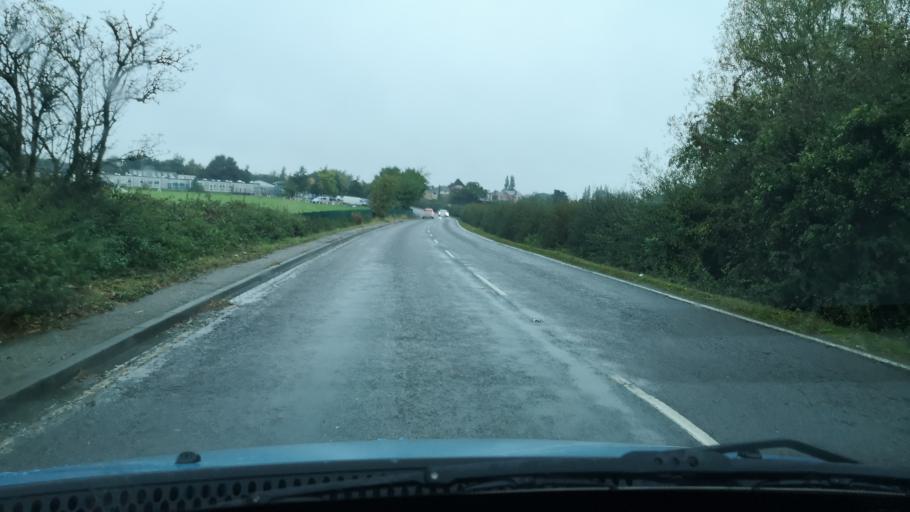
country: GB
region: England
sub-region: City and Borough of Wakefield
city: Low Ackworth
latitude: 53.6347
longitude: -1.3354
